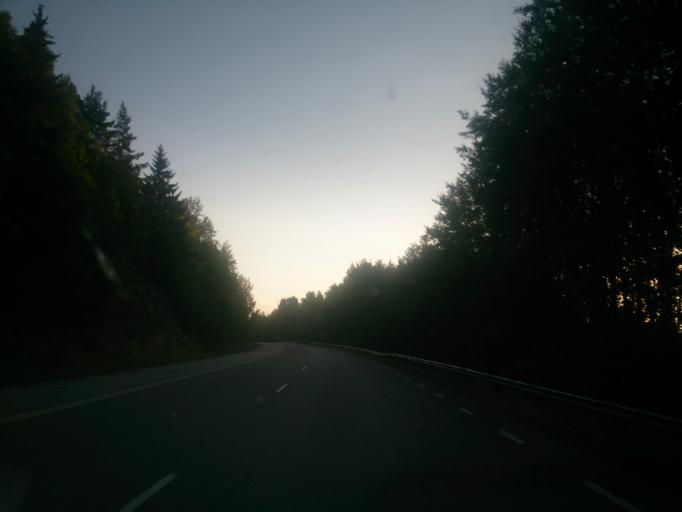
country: SE
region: Soedermanland
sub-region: Nykopings Kommun
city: Nykoping
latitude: 58.8319
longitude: 17.1099
